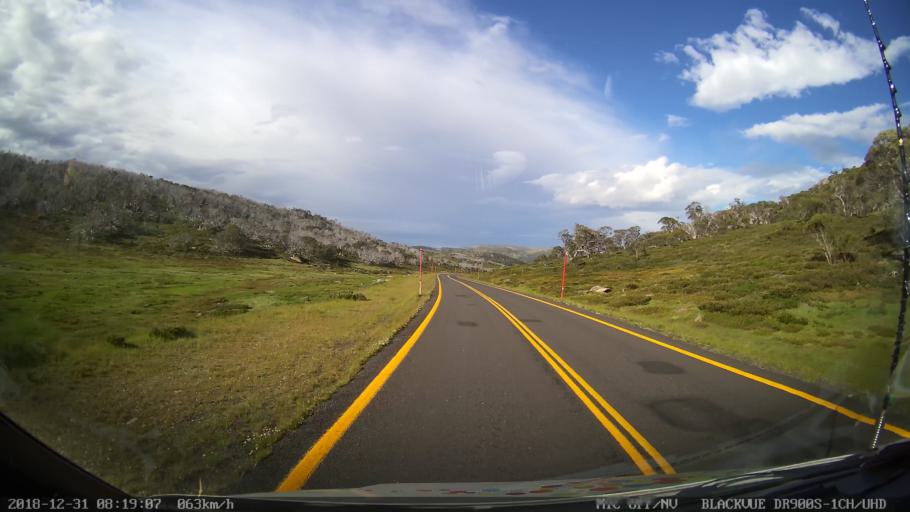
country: AU
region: New South Wales
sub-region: Snowy River
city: Jindabyne
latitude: -36.4175
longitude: 148.3892
